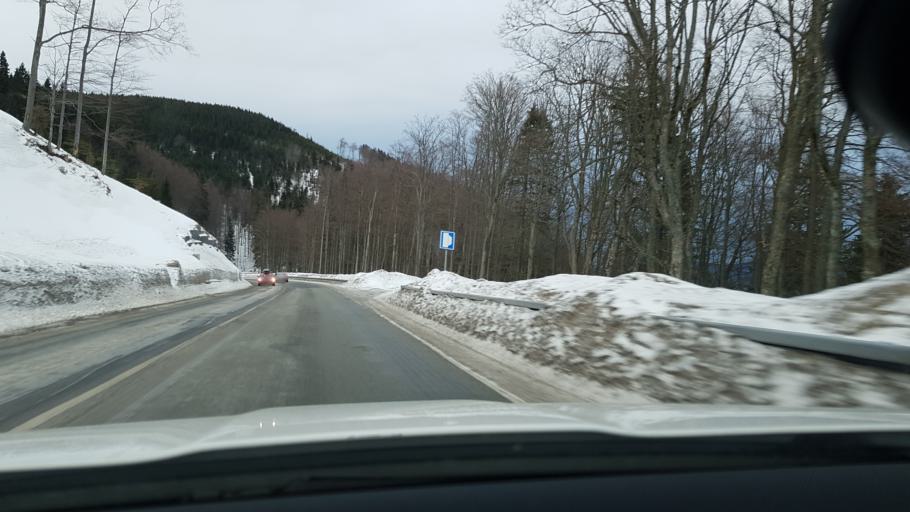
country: CZ
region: Olomoucky
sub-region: Okres Sumperk
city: Loucna nad Desnou
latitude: 50.1322
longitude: 17.1572
